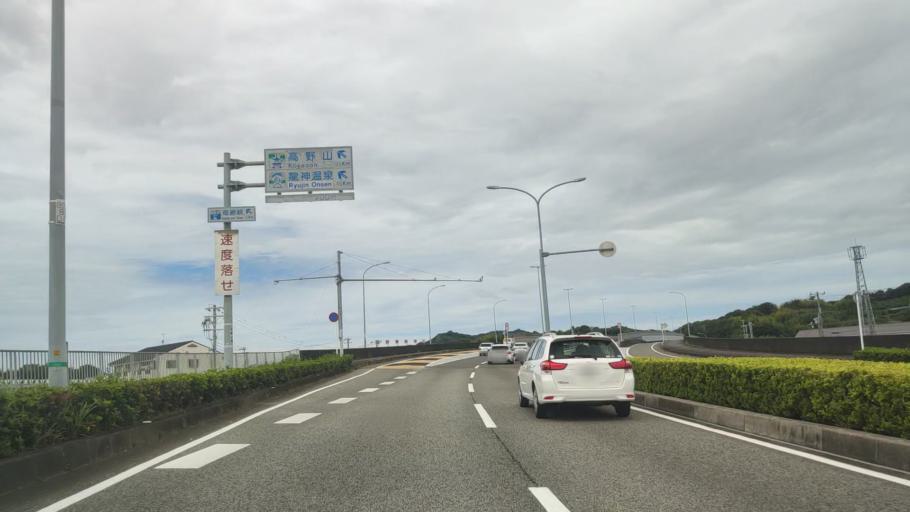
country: JP
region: Wakayama
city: Tanabe
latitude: 33.7412
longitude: 135.3886
